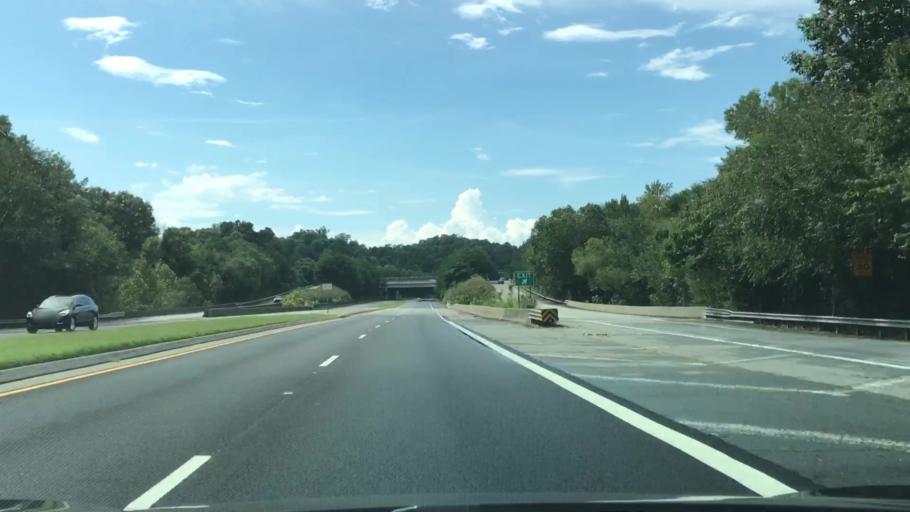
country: US
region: Georgia
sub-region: Gwinnett County
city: Lilburn
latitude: 33.9094
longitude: -84.0973
